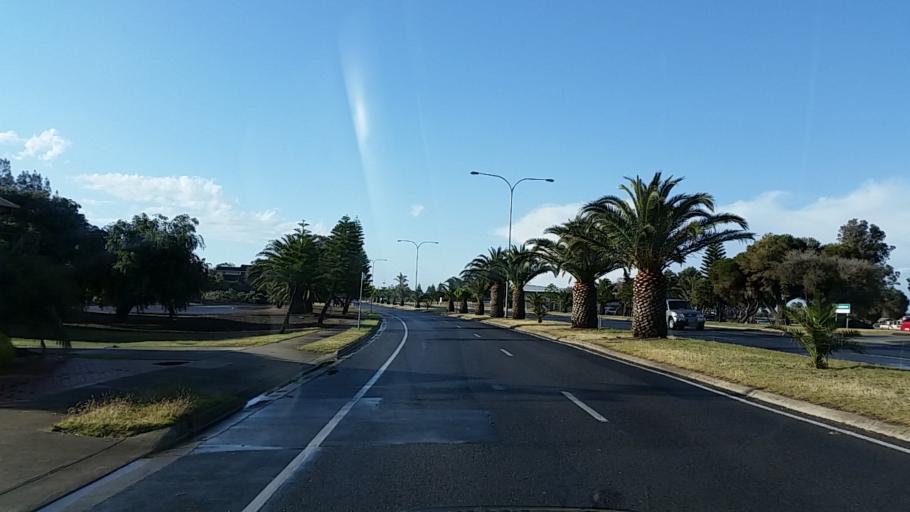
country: AU
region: South Australia
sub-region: Charles Sturt
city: West Lakes Shore
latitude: -34.8770
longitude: 138.4847
